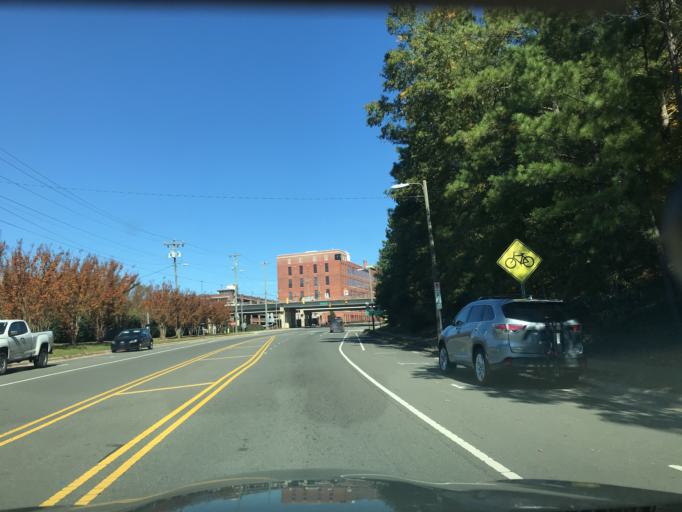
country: US
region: North Carolina
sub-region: Durham County
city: Durham
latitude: 35.9894
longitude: -78.9064
